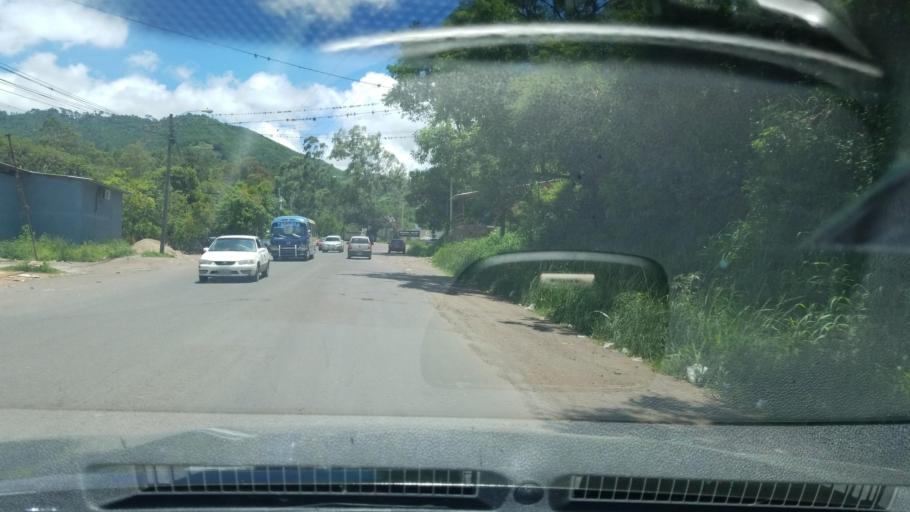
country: HN
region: Francisco Morazan
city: Rio Abajo
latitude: 14.1441
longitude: -87.2290
